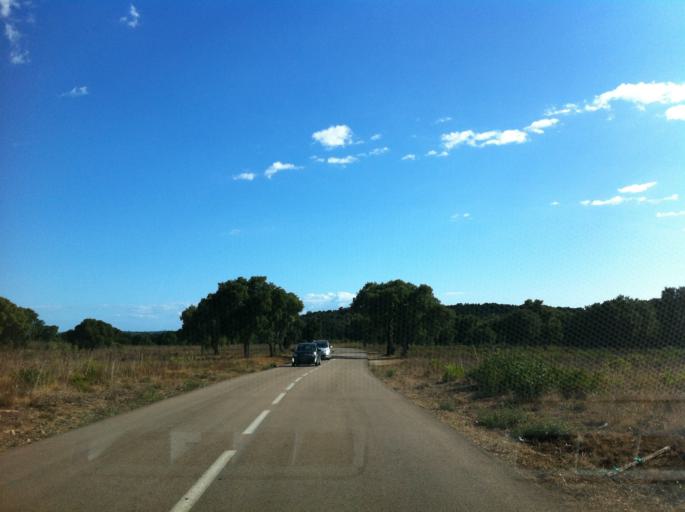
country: FR
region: Corsica
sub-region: Departement de la Corse-du-Sud
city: Porto-Vecchio
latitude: 41.6371
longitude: 9.2938
